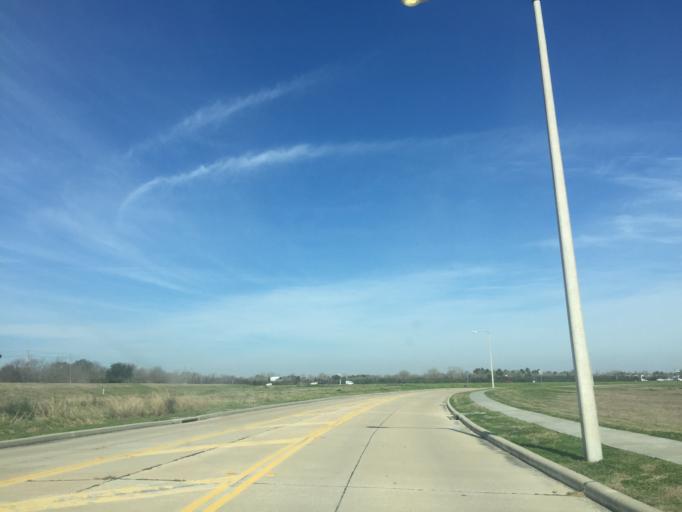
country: US
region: Texas
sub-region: Galveston County
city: Kemah
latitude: 29.5104
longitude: -95.0285
